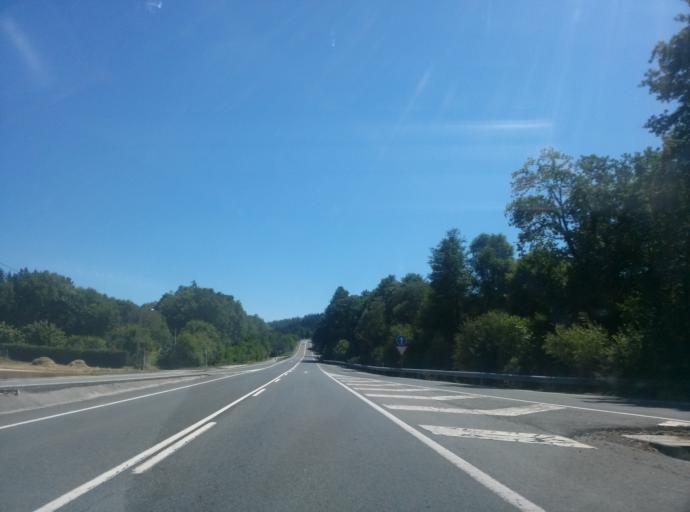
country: ES
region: Galicia
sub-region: Provincia de Lugo
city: Mos
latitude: 43.0920
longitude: -7.4785
